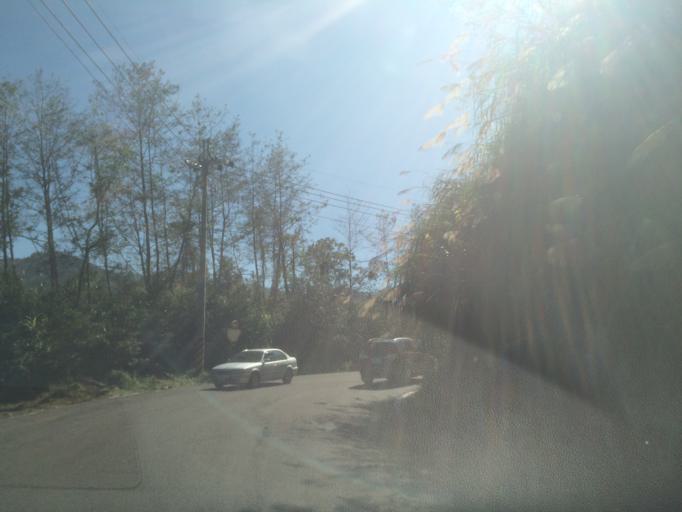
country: TW
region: Taiwan
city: Lugu
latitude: 23.6600
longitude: 120.7793
